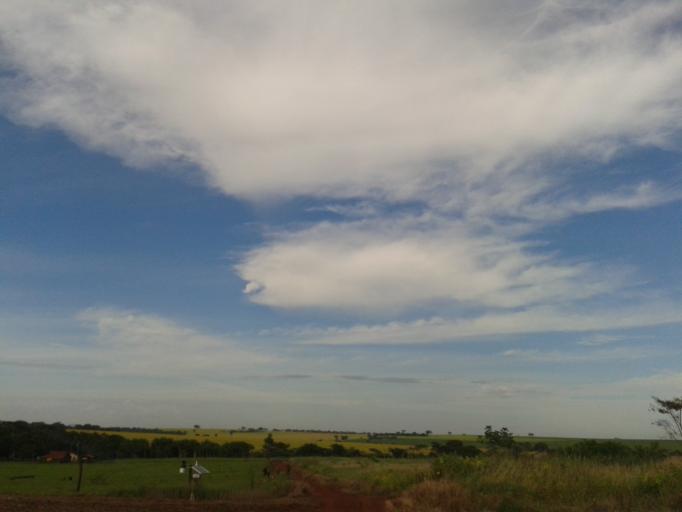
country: BR
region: Minas Gerais
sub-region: Capinopolis
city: Capinopolis
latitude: -18.6528
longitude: -49.6935
